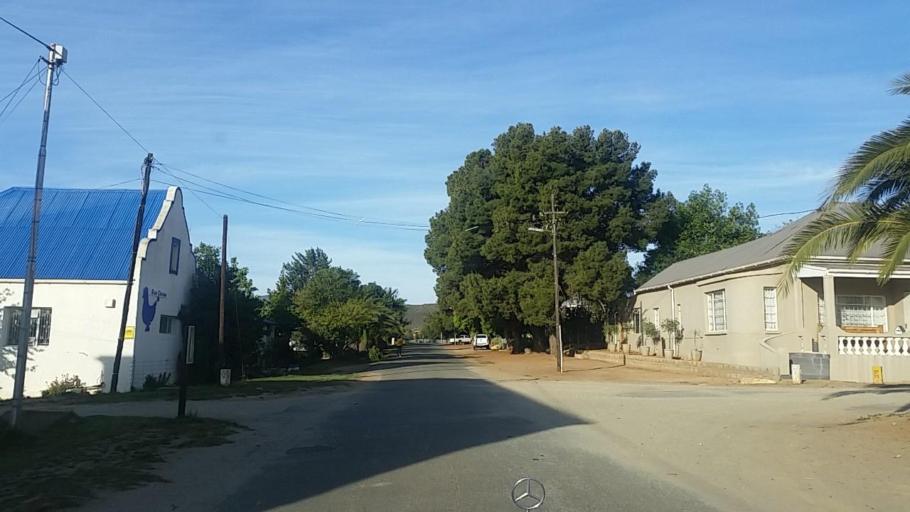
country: ZA
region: Western Cape
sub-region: Eden District Municipality
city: Knysna
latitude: -33.6544
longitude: 23.1277
